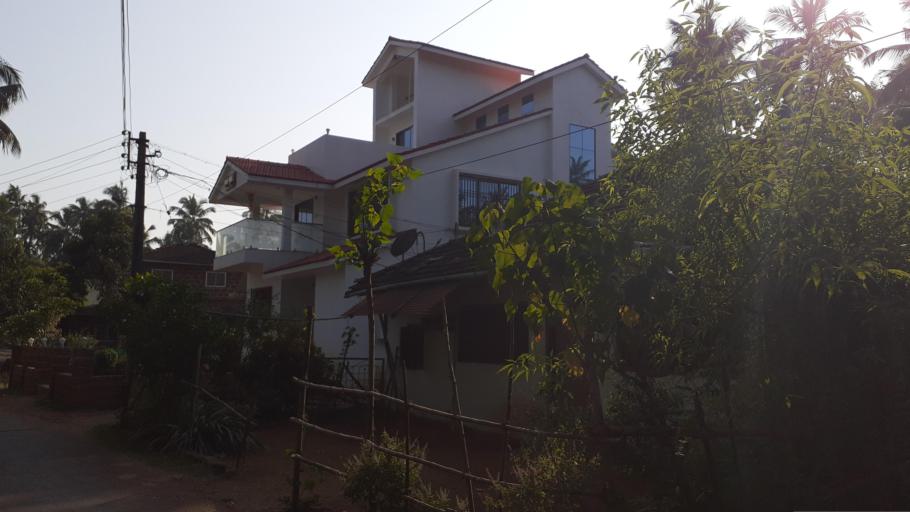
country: IN
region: Maharashtra
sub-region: Ratnagiri
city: Ratnagiri
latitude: 17.2154
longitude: 73.2479
